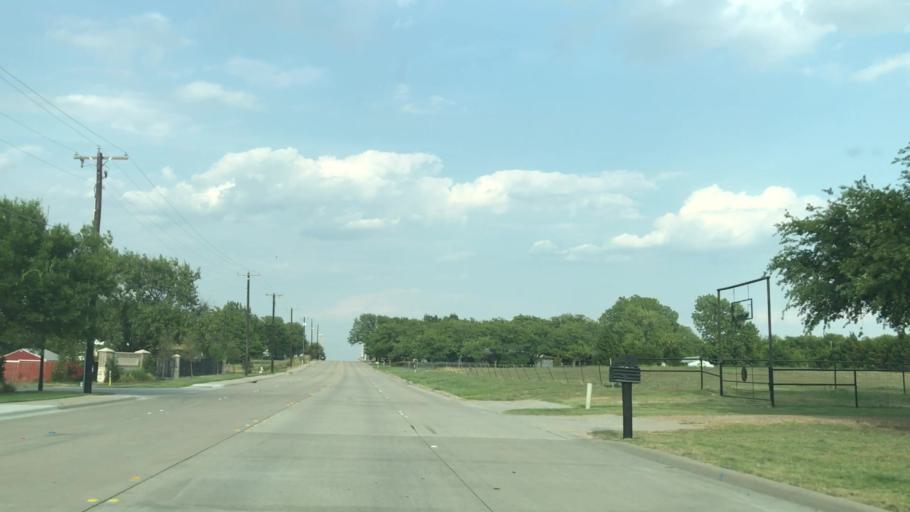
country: US
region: Texas
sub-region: Rockwall County
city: Rockwall
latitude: 32.9252
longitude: -96.4233
